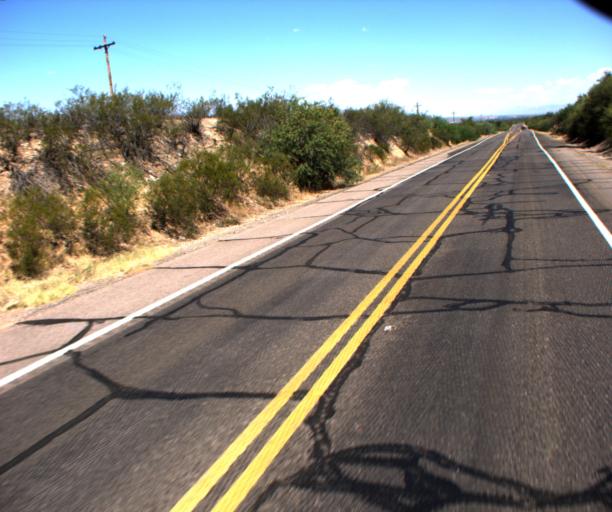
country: US
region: Arizona
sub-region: Pinal County
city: Mammoth
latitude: 32.7893
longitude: -110.6717
